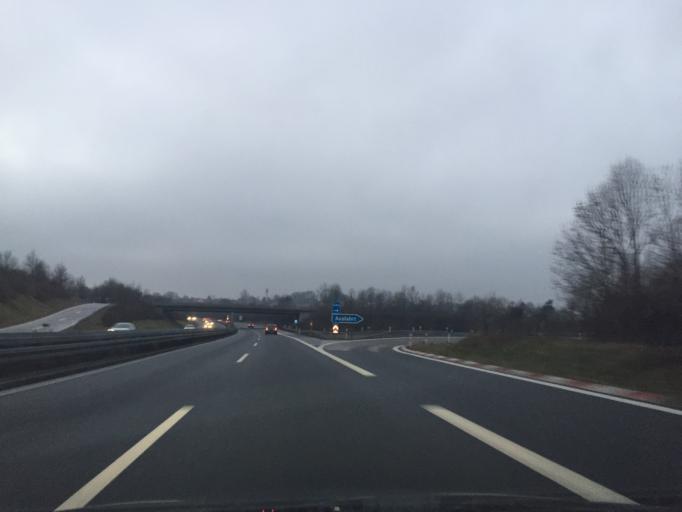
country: DE
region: Bavaria
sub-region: Upper Bavaria
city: Windach
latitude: 48.0662
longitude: 11.0080
